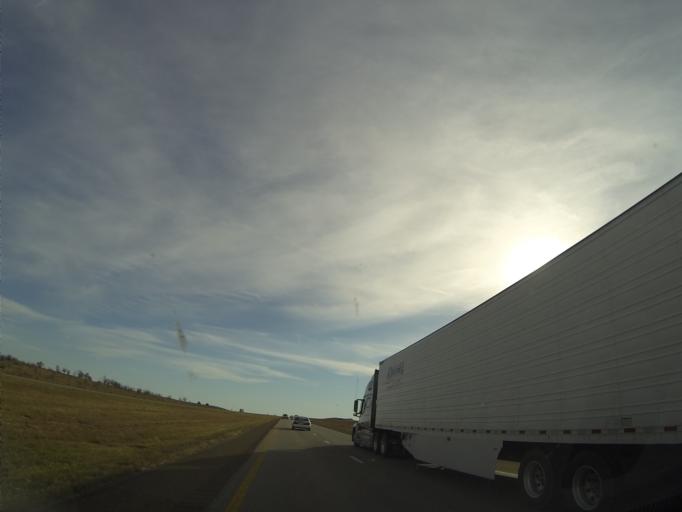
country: US
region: Kansas
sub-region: Ottawa County
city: Minneapolis
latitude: 38.9908
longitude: -97.6396
